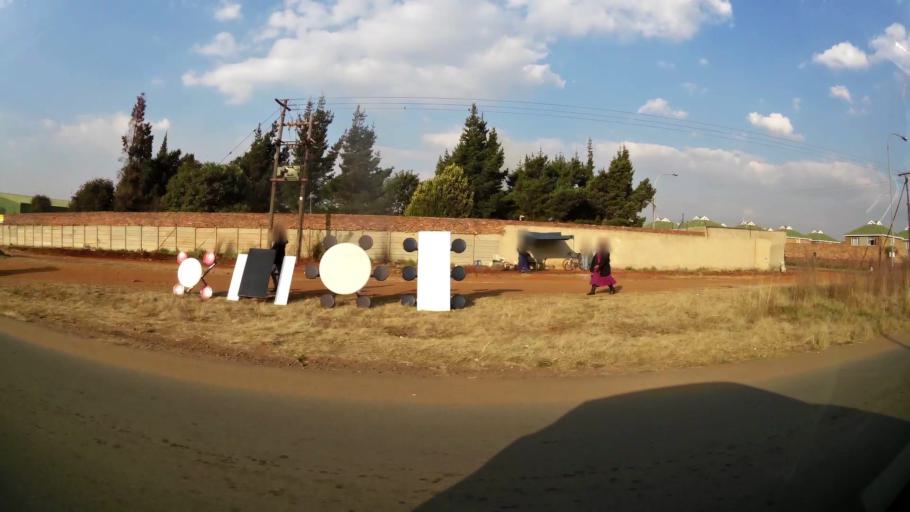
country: ZA
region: Gauteng
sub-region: Ekurhuleni Metropolitan Municipality
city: Benoni
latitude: -26.1105
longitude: 28.2956
